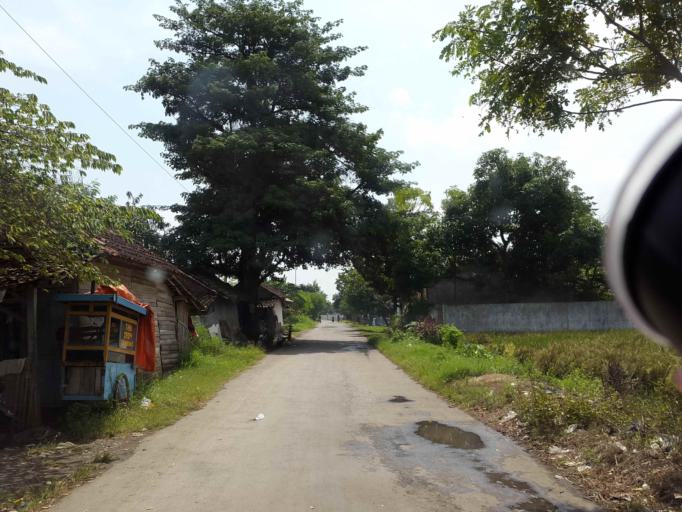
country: ID
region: Central Java
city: Pemalang
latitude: -6.9041
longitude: 109.3647
